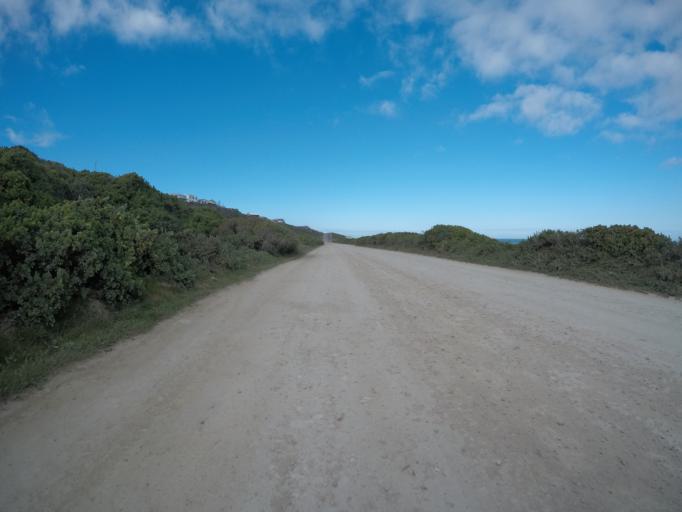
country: ZA
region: Western Cape
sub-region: Eden District Municipality
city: Riversdale
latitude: -34.4323
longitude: 21.3267
